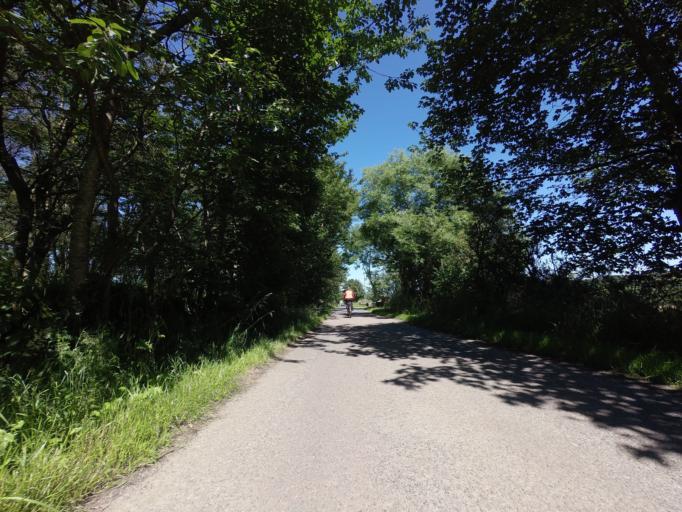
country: GB
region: Scotland
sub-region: Aberdeenshire
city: Macduff
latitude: 57.6502
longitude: -2.5038
